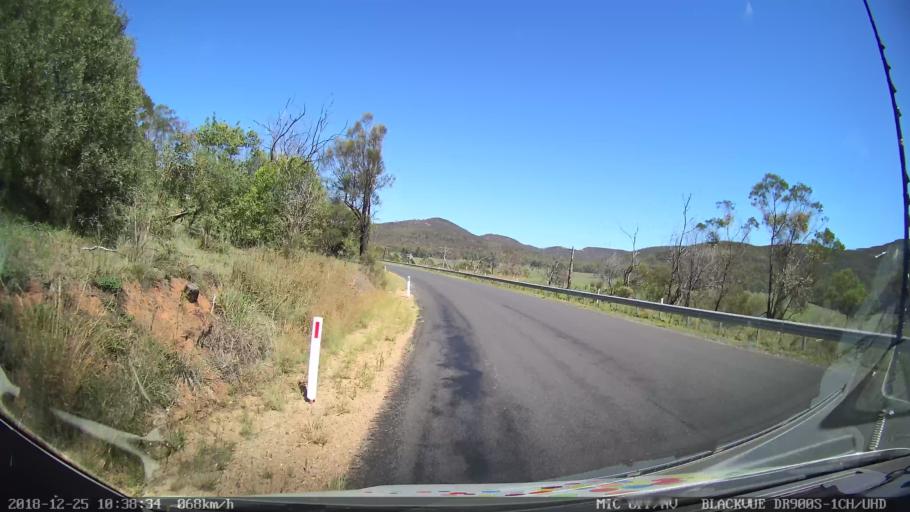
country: AU
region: New South Wales
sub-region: Upper Hunter Shire
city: Merriwa
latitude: -32.4028
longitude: 150.3666
